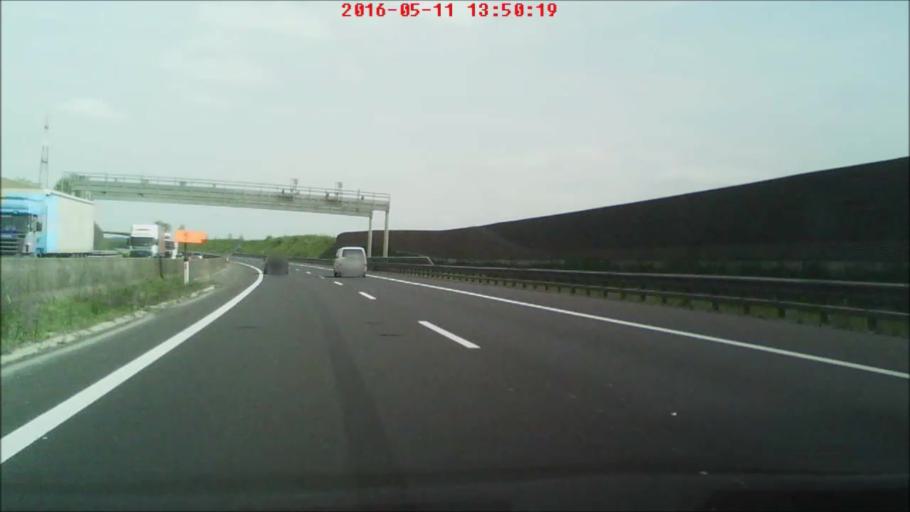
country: AT
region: Upper Austria
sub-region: Politischer Bezirk Vocklabruck
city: Wolfsegg am Hausruck
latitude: 48.1794
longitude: 13.6962
